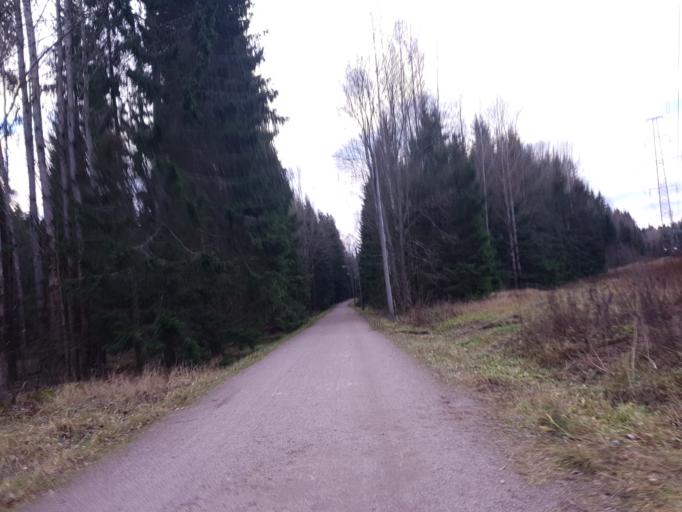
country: FI
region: Uusimaa
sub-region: Helsinki
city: Teekkarikylae
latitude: 60.2713
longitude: 24.9019
